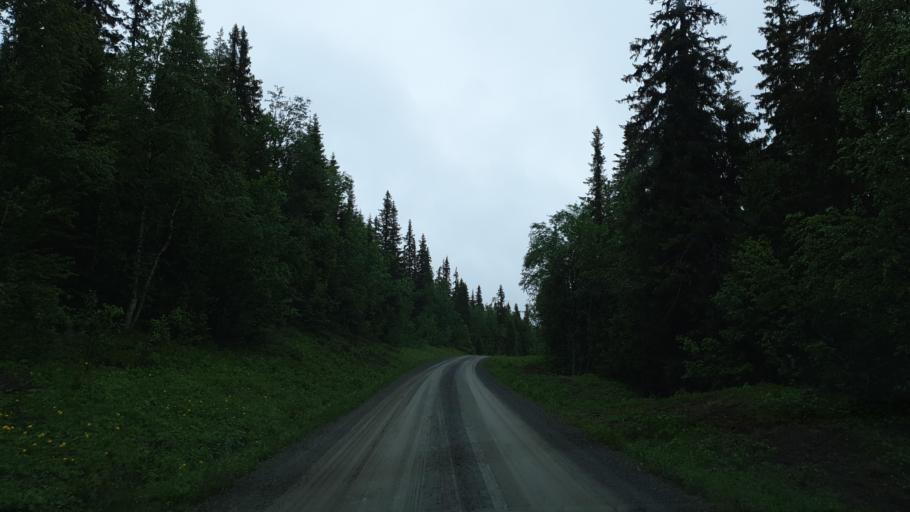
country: SE
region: Vaesterbotten
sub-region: Vilhelmina Kommun
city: Sjoberg
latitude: 65.3291
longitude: 15.9150
